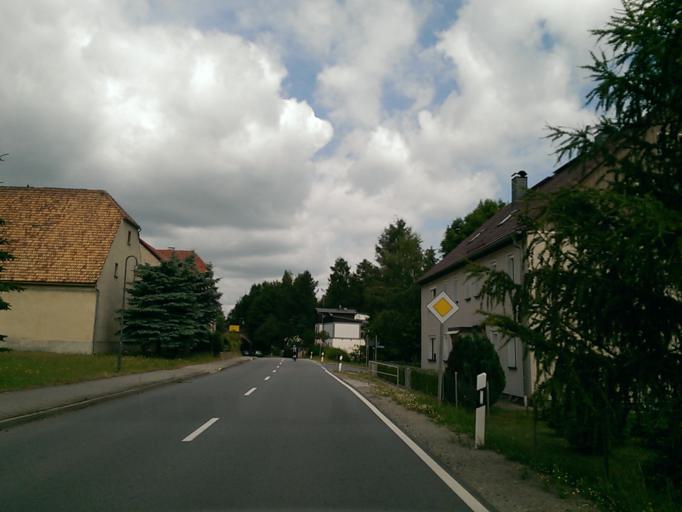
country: DE
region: Saxony
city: Eibau
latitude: 50.9673
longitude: 14.7110
